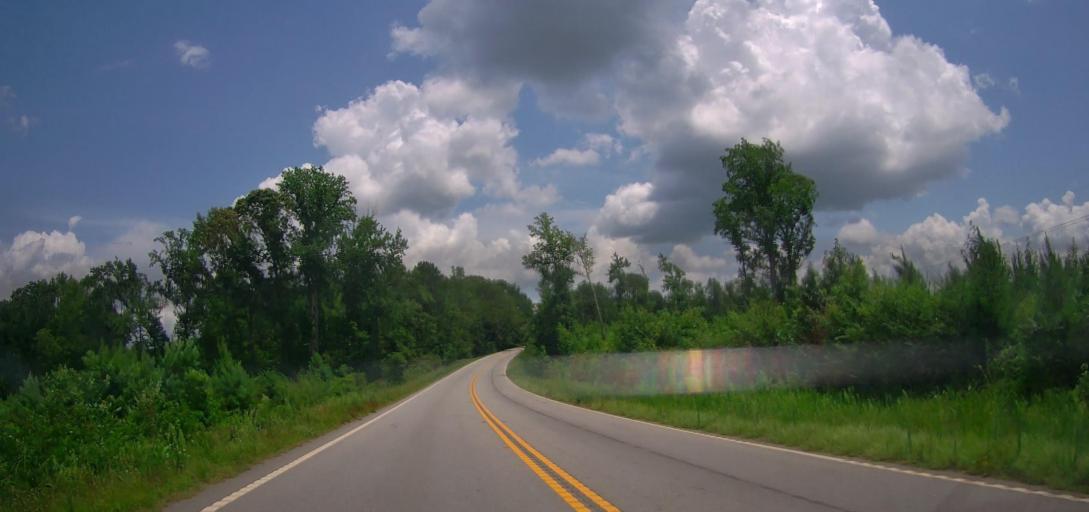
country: US
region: Georgia
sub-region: Meriwether County
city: Greenville
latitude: 33.0286
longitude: -84.6913
